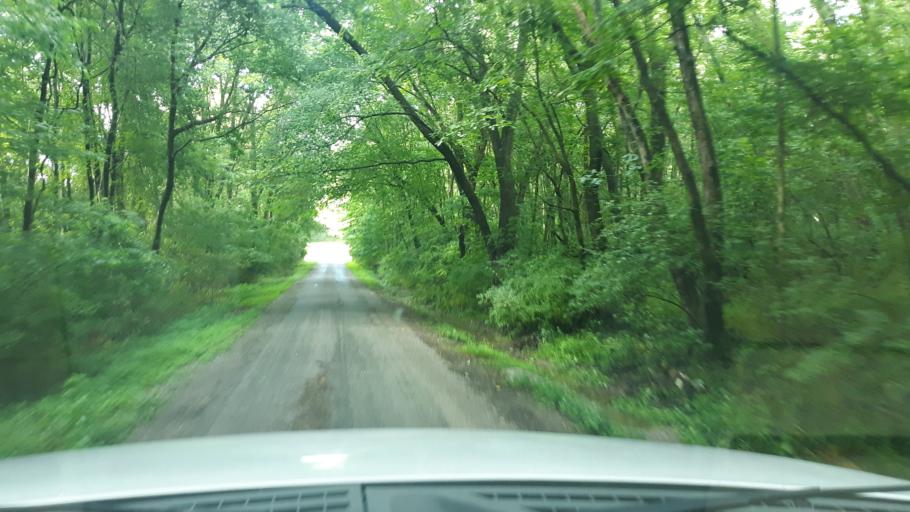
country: US
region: Illinois
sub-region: Saline County
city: Harrisburg
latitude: 37.8458
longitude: -88.6115
